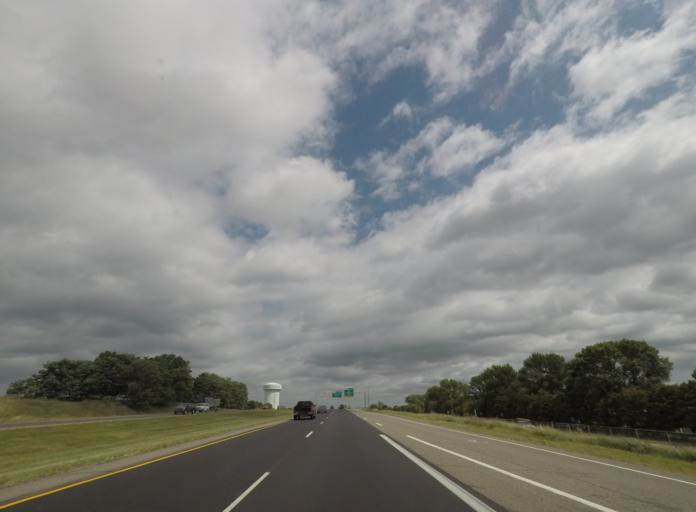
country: US
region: Iowa
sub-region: Linn County
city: Cedar Rapids
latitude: 41.9267
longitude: -91.6513
